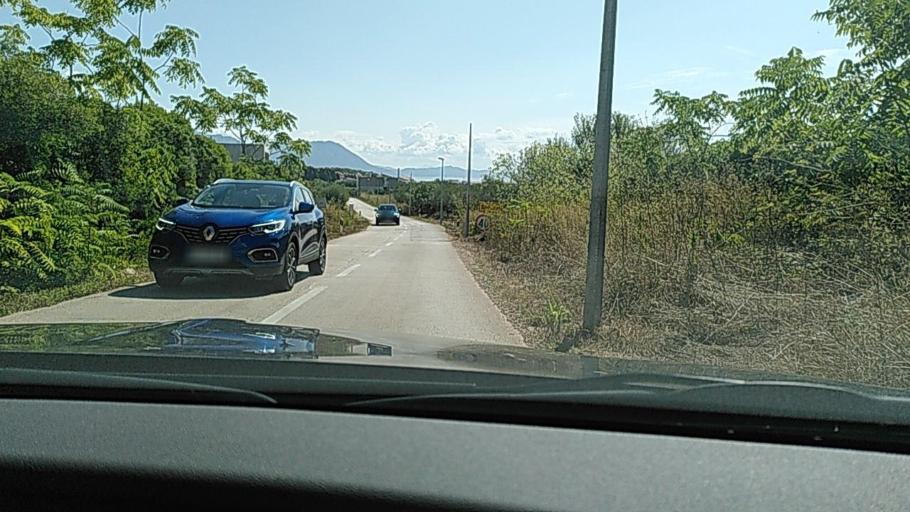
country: HR
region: Dubrovacko-Neretvanska
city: Orebic
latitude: 43.1286
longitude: 17.1769
